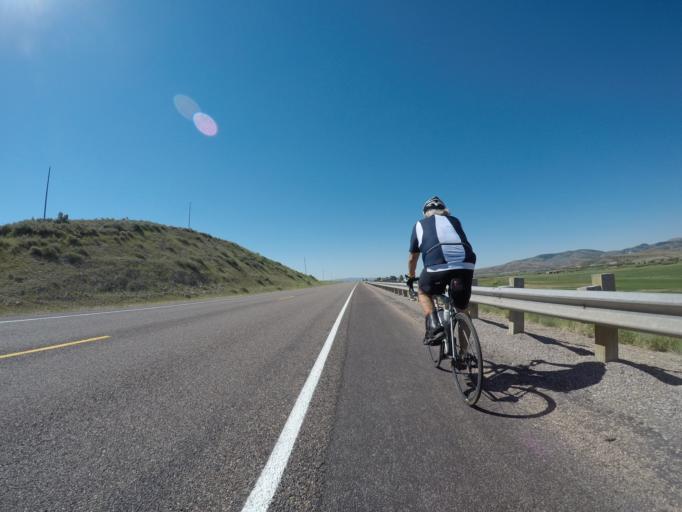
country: US
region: Idaho
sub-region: Bear Lake County
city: Montpelier
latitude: 42.3777
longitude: -111.0530
